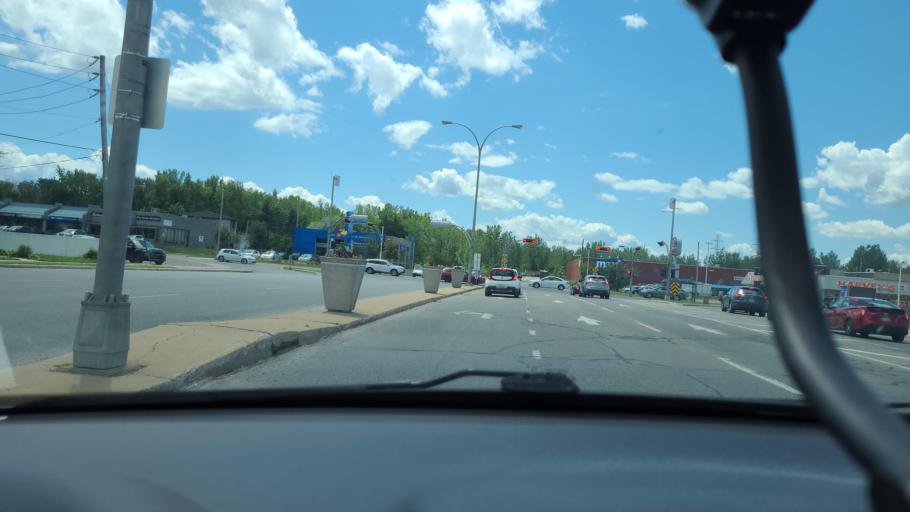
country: CA
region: Quebec
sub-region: Laval
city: Laval
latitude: 45.6070
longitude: -73.7315
